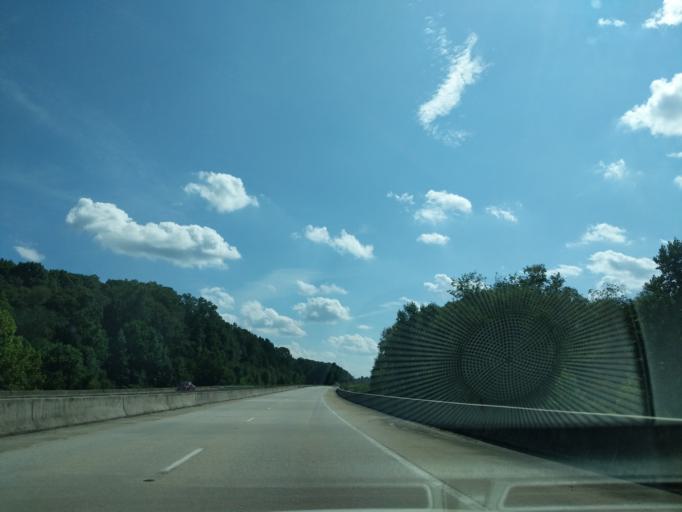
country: US
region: Georgia
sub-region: Banks County
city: Homer
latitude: 34.3274
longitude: -83.4650
